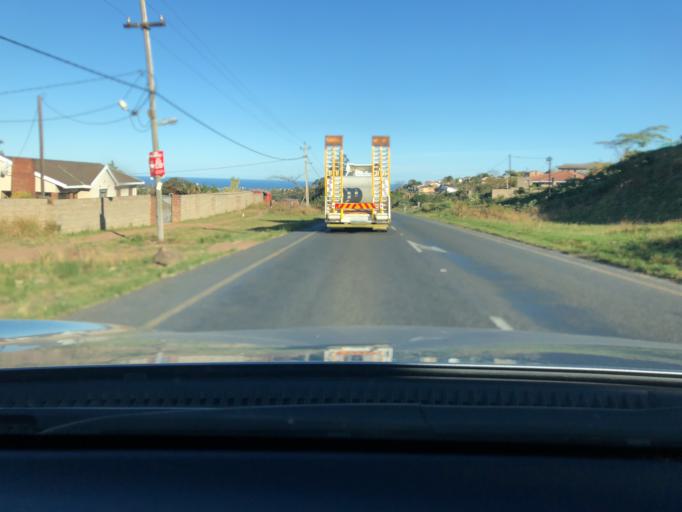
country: ZA
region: KwaZulu-Natal
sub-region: eThekwini Metropolitan Municipality
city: Umkomaas
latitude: -30.0129
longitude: 30.8063
